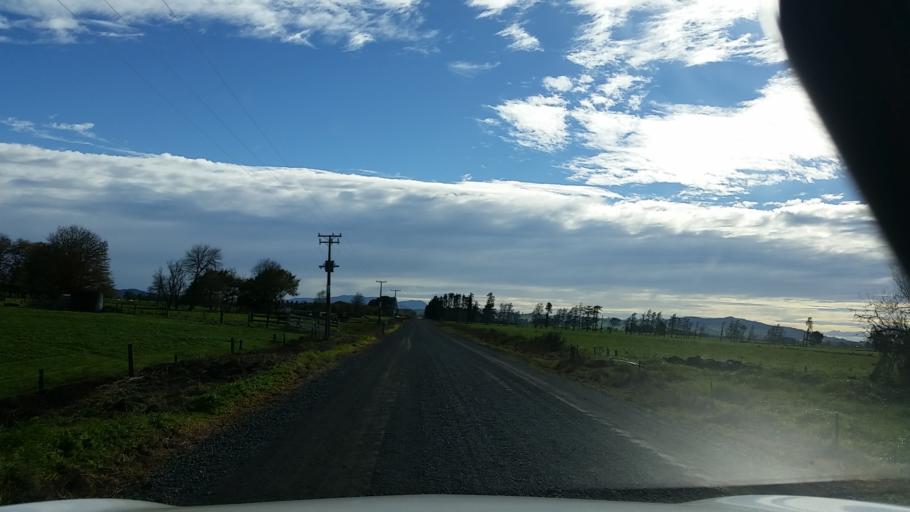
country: NZ
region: Waikato
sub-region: Hamilton City
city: Hamilton
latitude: -37.6651
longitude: 175.4386
